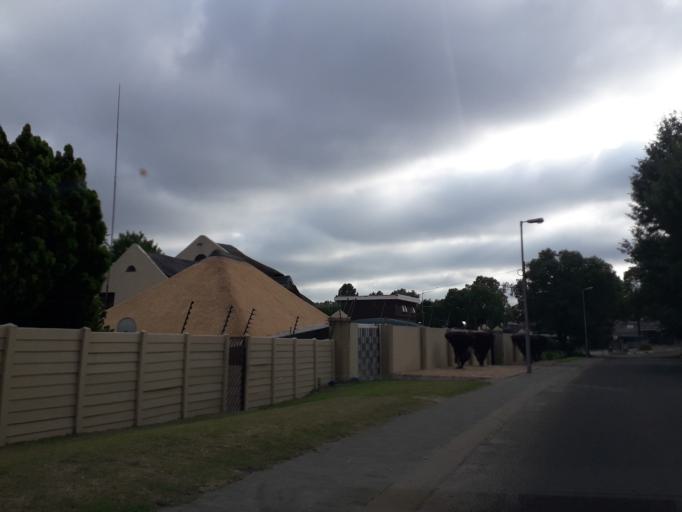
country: ZA
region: Gauteng
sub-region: City of Johannesburg Metropolitan Municipality
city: Roodepoort
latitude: -26.1024
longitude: 27.9598
